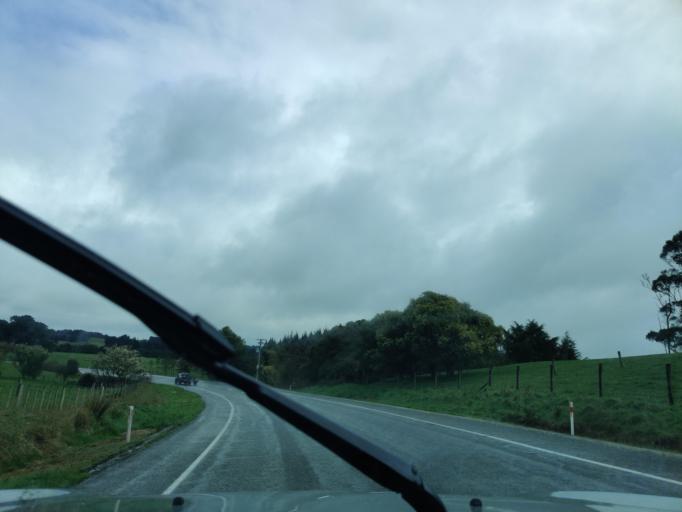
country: NZ
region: Manawatu-Wanganui
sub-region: Palmerston North City
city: Palmerston North
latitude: -40.0817
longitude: 176.1960
